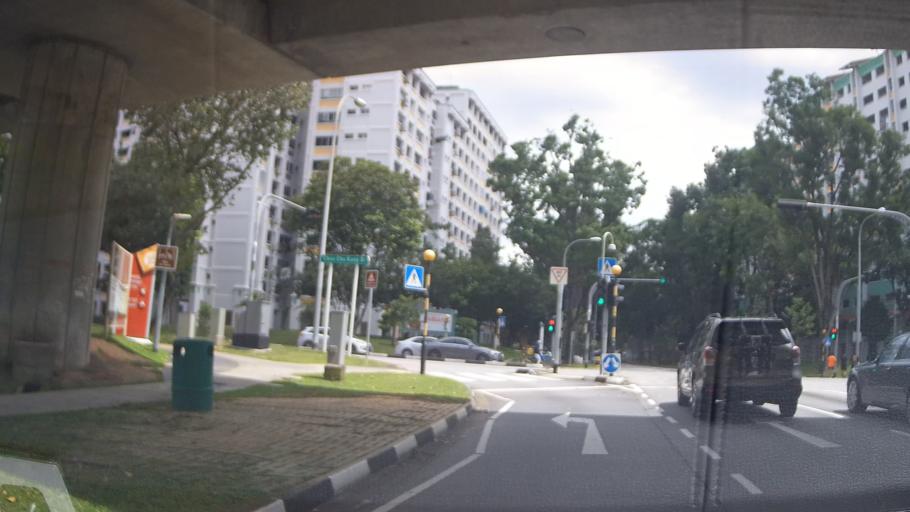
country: MY
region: Johor
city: Johor Bahru
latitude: 1.3925
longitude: 103.7448
